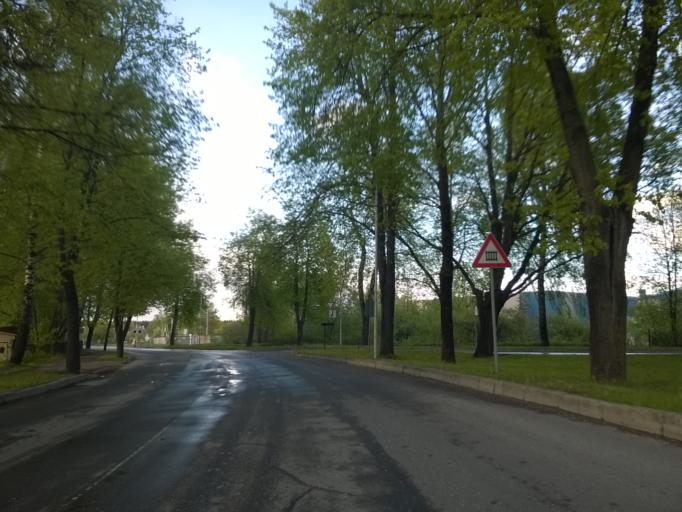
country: LV
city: Tireli
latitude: 56.9484
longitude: 23.6315
